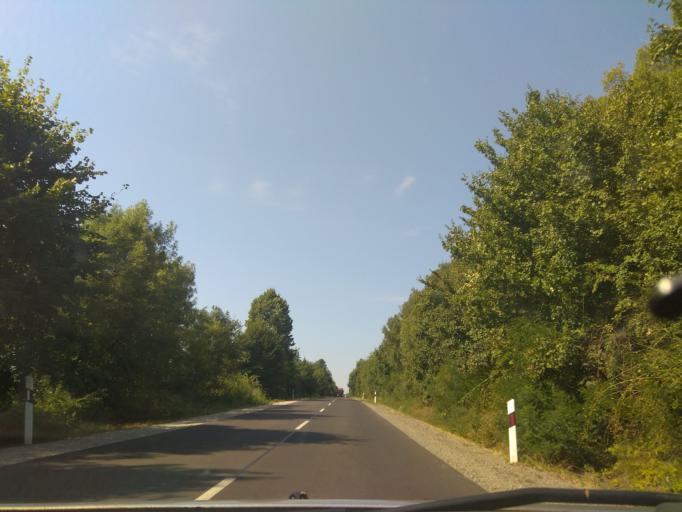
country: HU
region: Borsod-Abauj-Zemplen
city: Harsany
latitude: 47.9366
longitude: 20.7375
